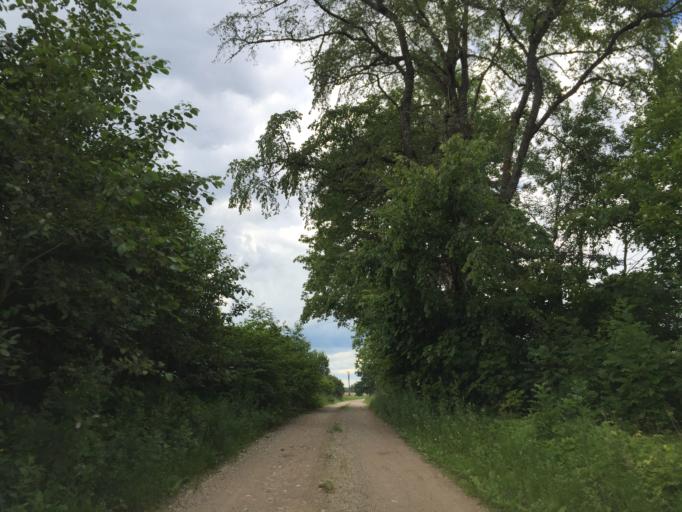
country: LV
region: Ogre
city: Jumprava
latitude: 56.8441
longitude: 25.0515
